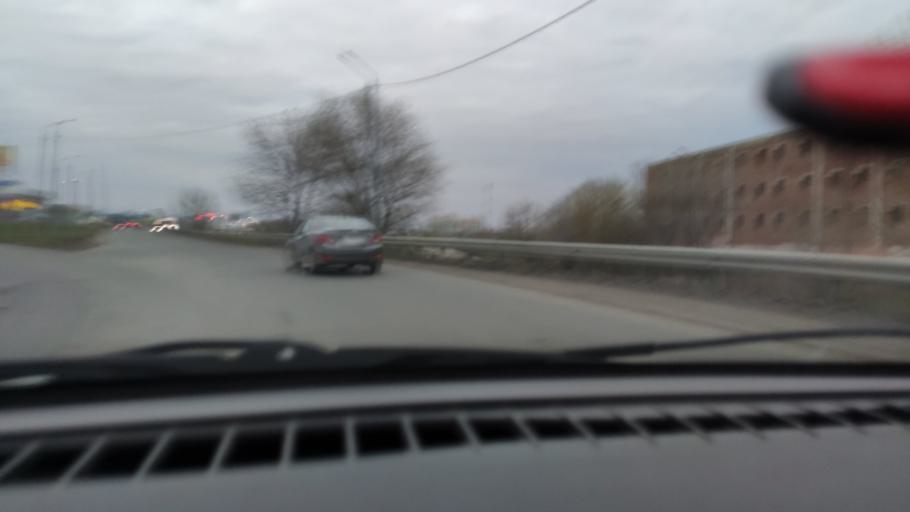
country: RU
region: Orenburg
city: Orenburg
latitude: 51.8498
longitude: 55.1430
